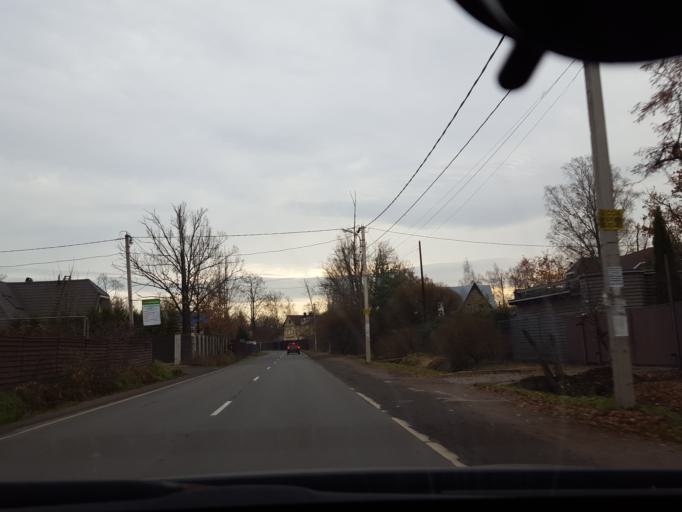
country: RU
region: St.-Petersburg
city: Shuvalovo
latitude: 60.0454
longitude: 30.2961
